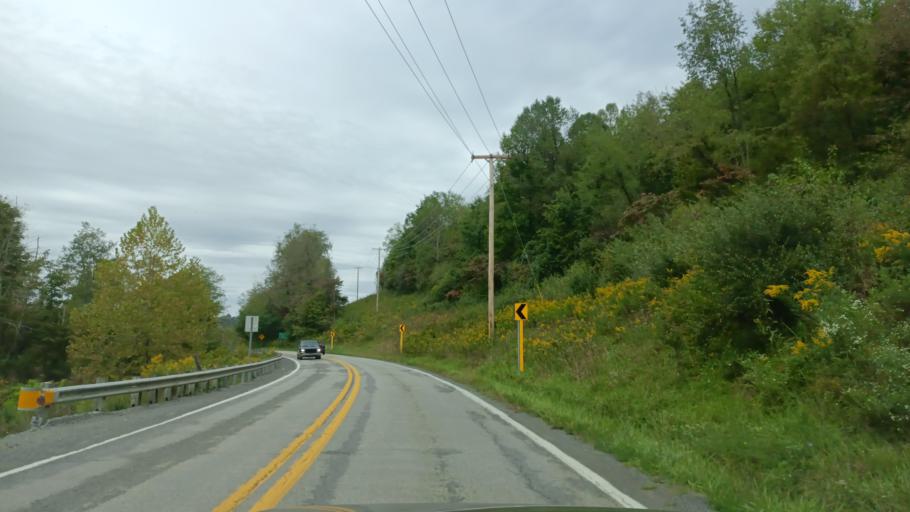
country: US
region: West Virginia
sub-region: Taylor County
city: Grafton
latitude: 39.3365
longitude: -79.8519
